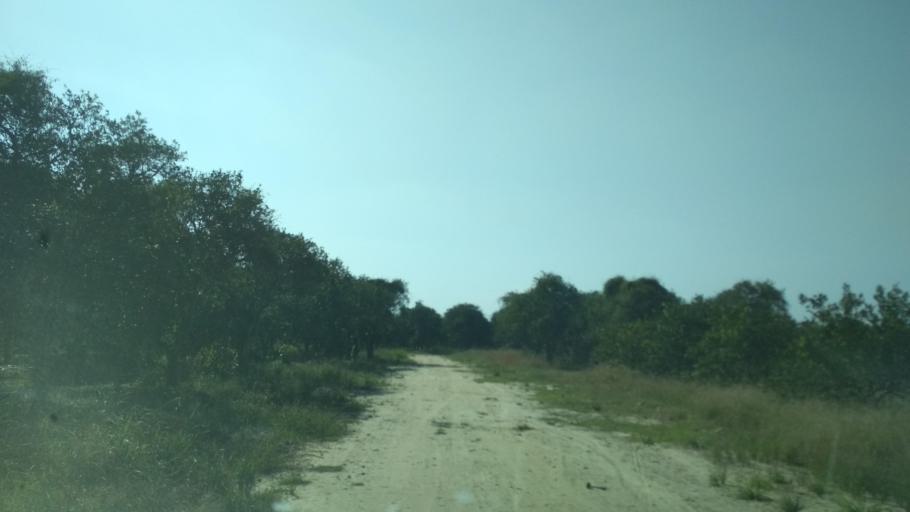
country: MX
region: Veracruz
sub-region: Martinez de la Torre
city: El Progreso
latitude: 20.0858
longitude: -97.0208
